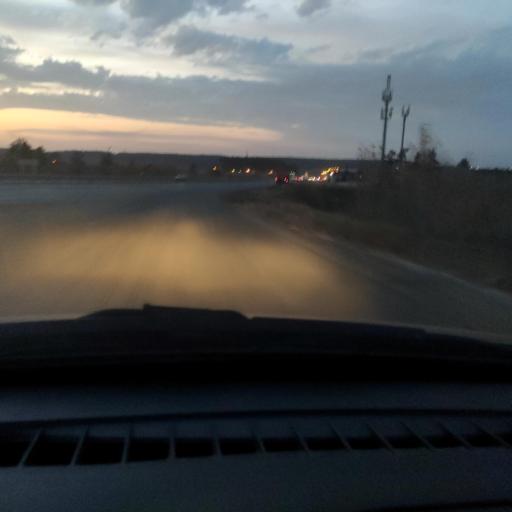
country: RU
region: Samara
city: Zhigulevsk
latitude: 53.5203
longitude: 49.5323
